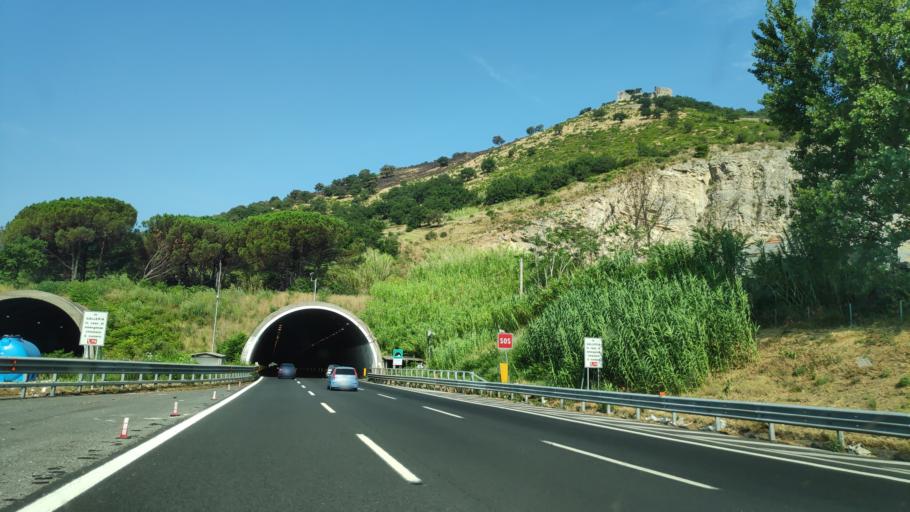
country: IT
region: Campania
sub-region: Provincia di Salerno
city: Lanzara
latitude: 40.7724
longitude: 14.6614
